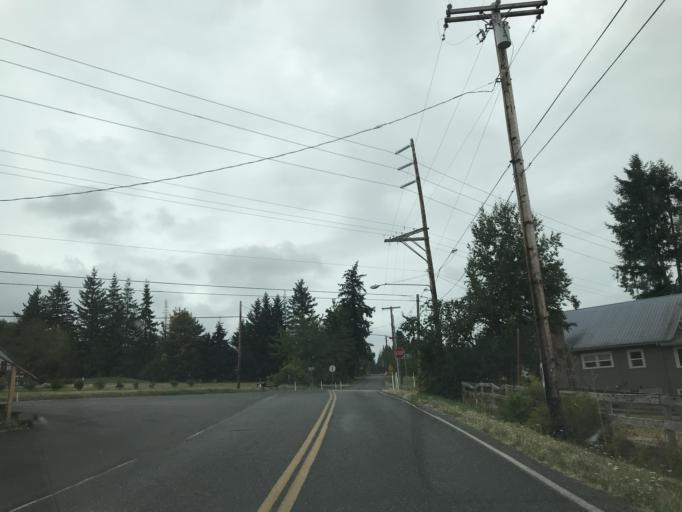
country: US
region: Washington
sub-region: Whatcom County
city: Sudden Valley
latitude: 48.8151
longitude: -122.3326
